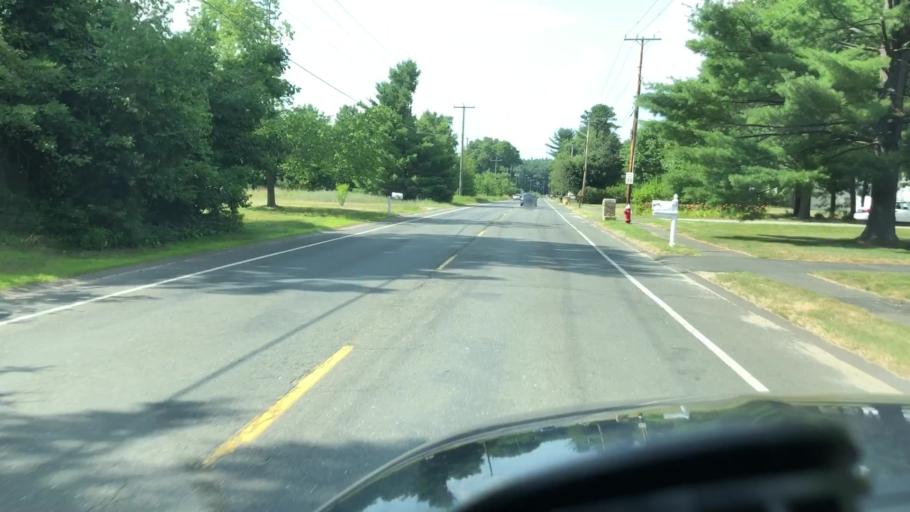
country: US
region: Massachusetts
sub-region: Hampshire County
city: Southampton
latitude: 42.2095
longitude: -72.6899
